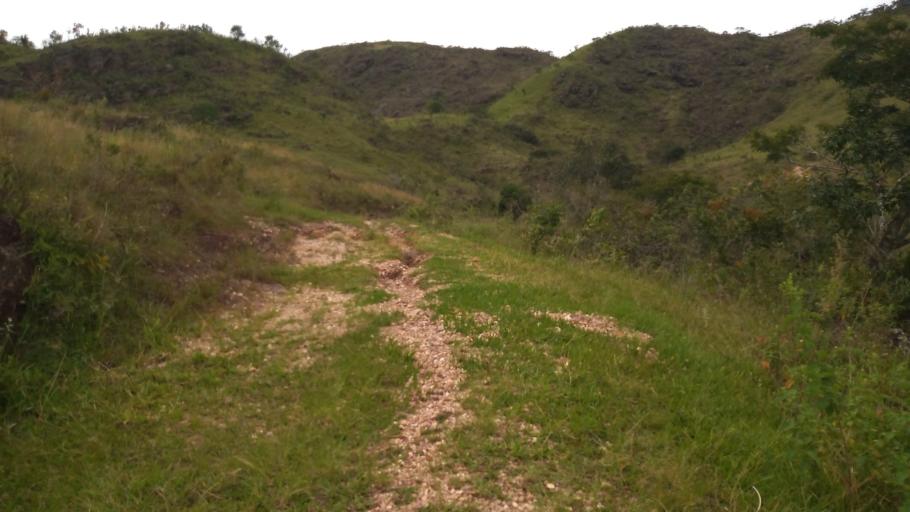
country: BR
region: Minas Gerais
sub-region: Sao Joao Del Rei
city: Sao Joao del Rei
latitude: -21.1258
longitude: -44.2711
